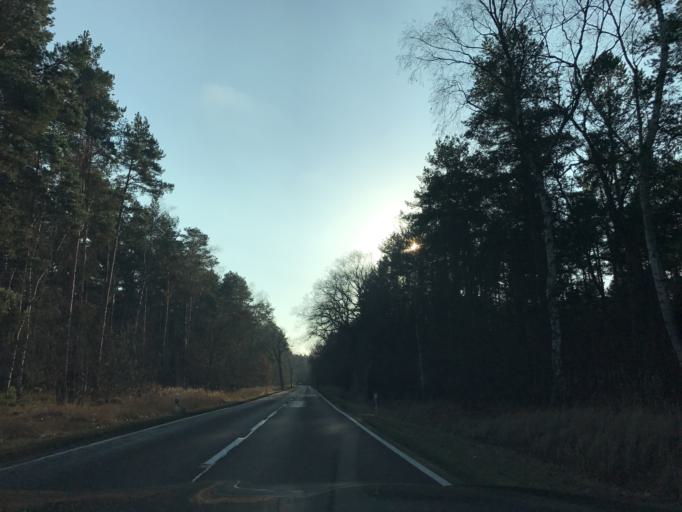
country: DE
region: Brandenburg
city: Wenzlow
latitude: 52.3514
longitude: 12.5009
